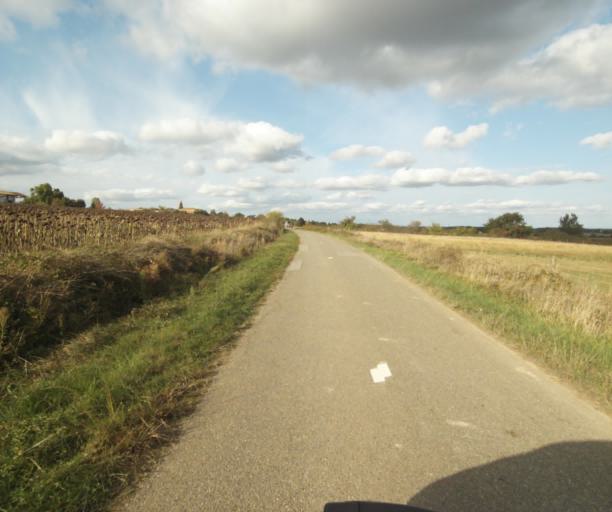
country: FR
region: Midi-Pyrenees
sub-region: Departement de la Haute-Garonne
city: Launac
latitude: 43.8368
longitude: 1.1205
